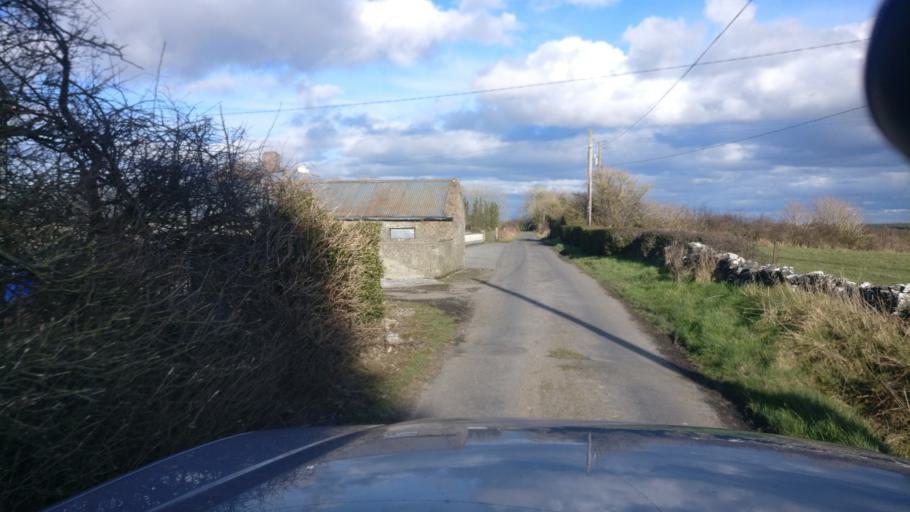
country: IE
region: Connaught
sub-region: County Galway
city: Loughrea
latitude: 53.2030
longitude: -8.4017
